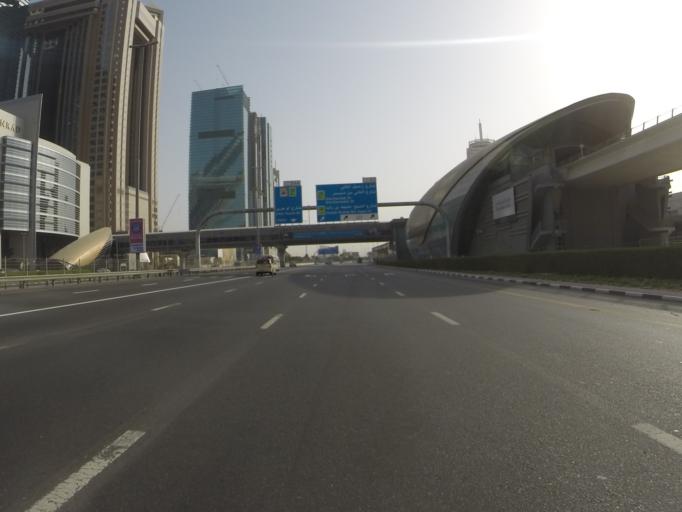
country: AE
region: Ash Shariqah
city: Sharjah
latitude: 25.2243
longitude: 55.2843
